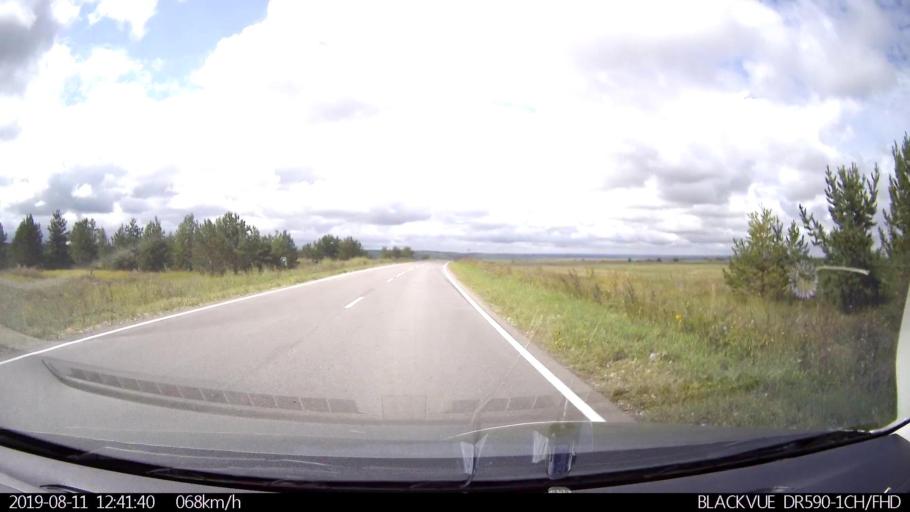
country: RU
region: Ulyanovsk
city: Ignatovka
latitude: 53.8420
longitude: 47.7615
